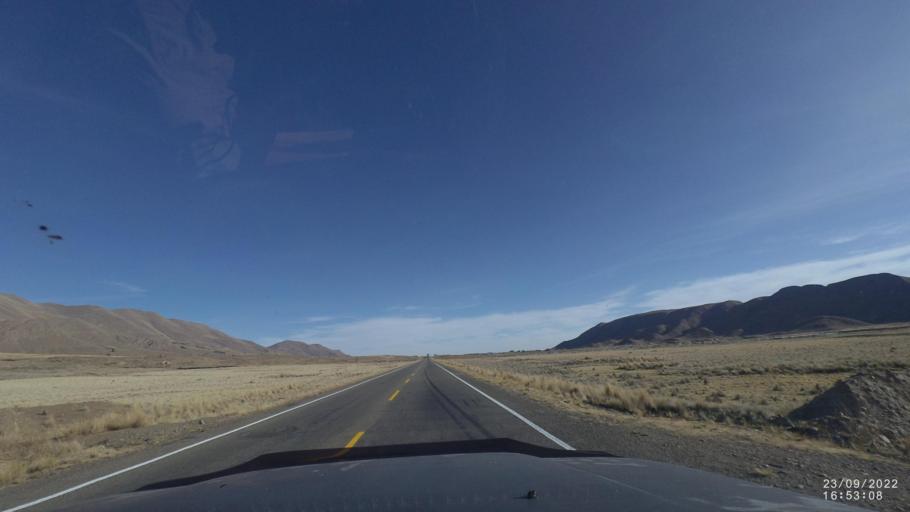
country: BO
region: Oruro
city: Poopo
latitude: -18.4426
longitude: -66.9722
